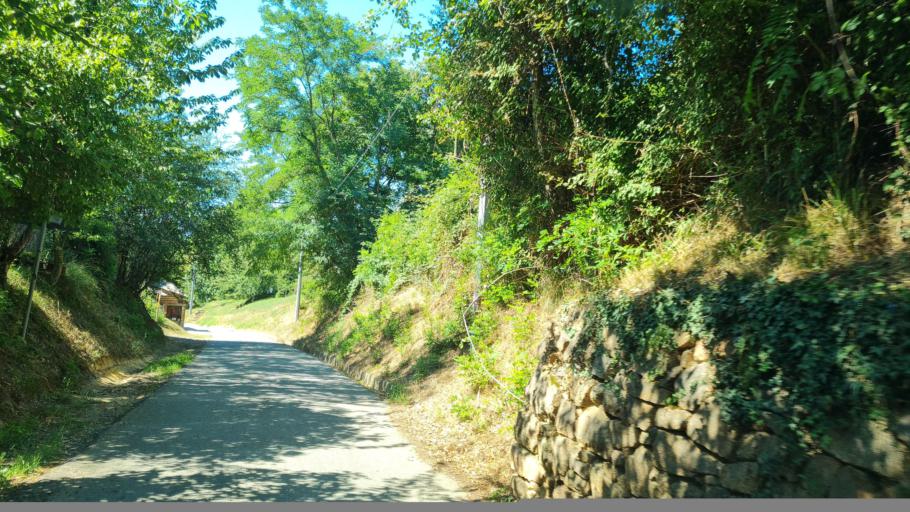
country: IT
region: Piedmont
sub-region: Provincia di Biella
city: Masserano
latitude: 45.5865
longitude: 8.2201
